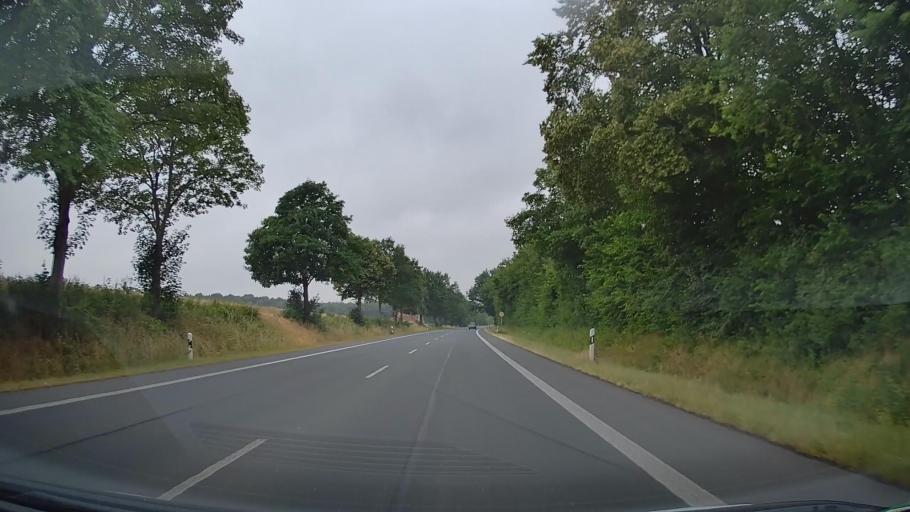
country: DE
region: North Rhine-Westphalia
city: Rahden
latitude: 52.4298
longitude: 8.6004
